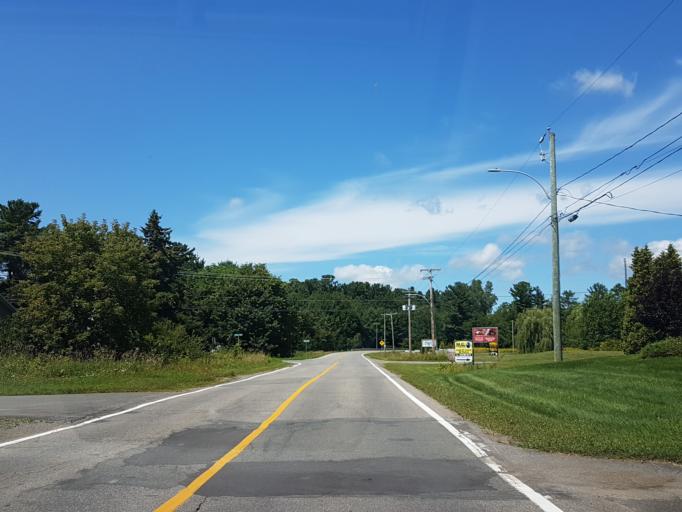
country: CA
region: Quebec
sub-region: Mauricie
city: Nicolet
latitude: 46.2895
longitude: -72.6861
